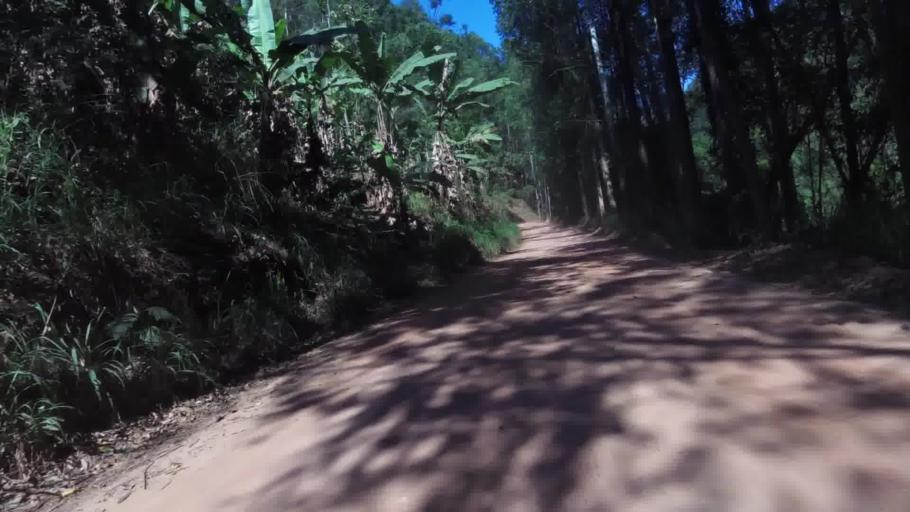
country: BR
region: Espirito Santo
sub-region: Alfredo Chaves
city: Alfredo Chaves
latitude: -20.6449
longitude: -40.7921
